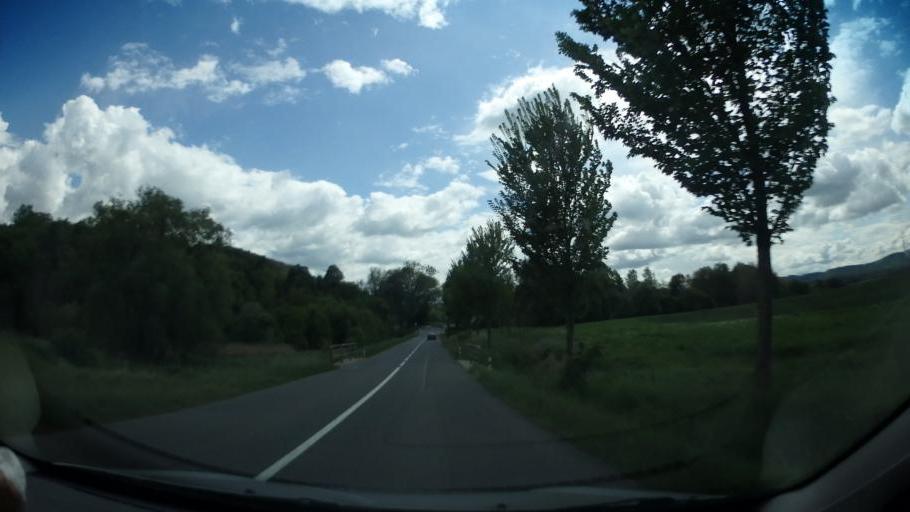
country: CZ
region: Pardubicky
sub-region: Okres Svitavy
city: Moravska Trebova
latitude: 49.7209
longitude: 16.6399
